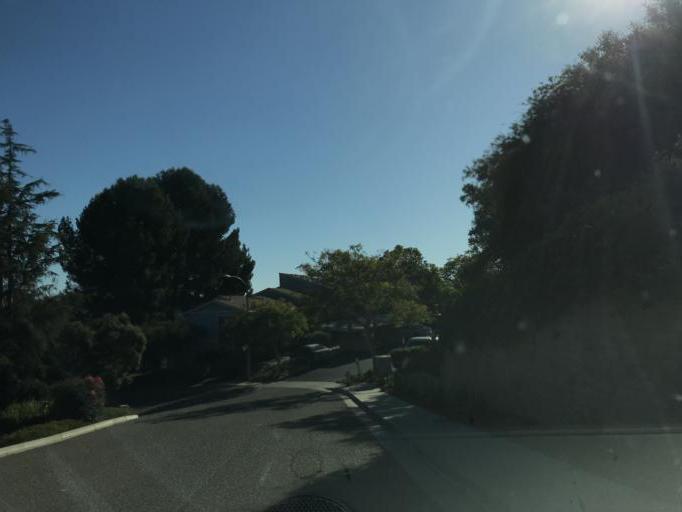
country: US
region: California
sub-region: Santa Barbara County
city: Goleta
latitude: 34.4471
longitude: -119.7811
